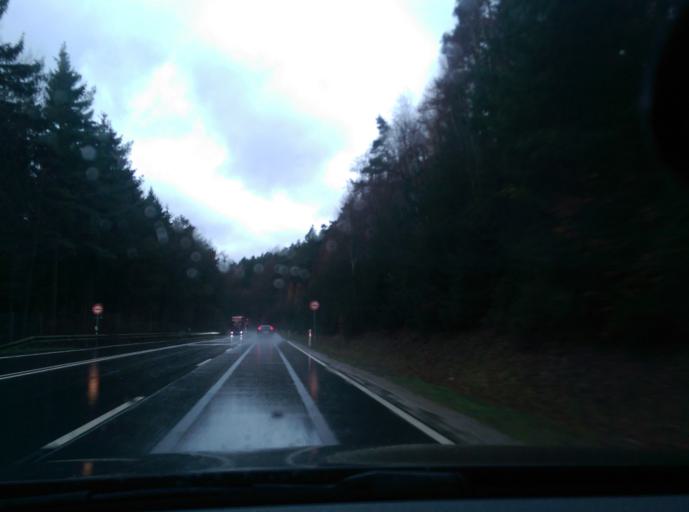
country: DE
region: Thuringia
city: Gerstungen
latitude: 51.0192
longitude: 10.0495
